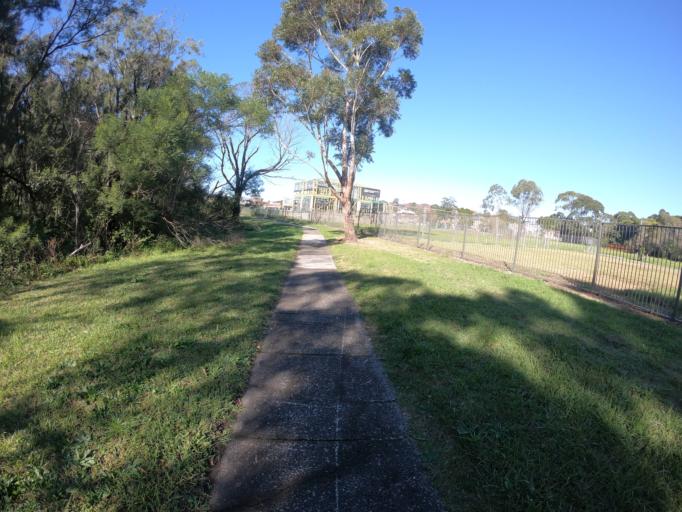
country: AU
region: New South Wales
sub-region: Wollongong
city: Mount Saint Thomas
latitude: -34.4421
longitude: 150.8564
